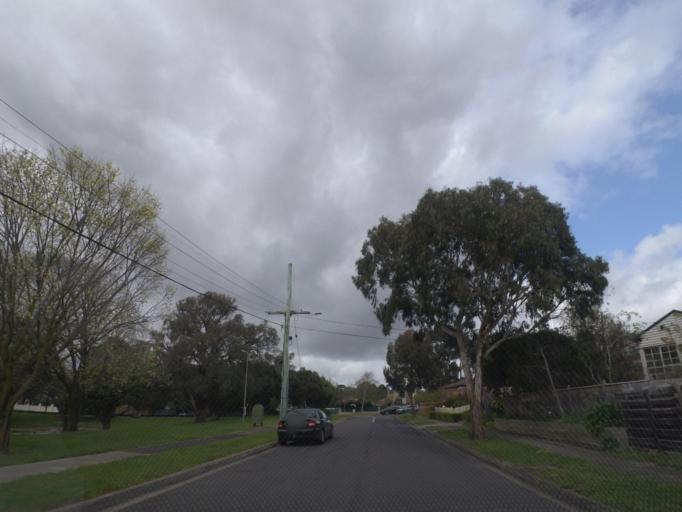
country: AU
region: Victoria
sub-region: Whitehorse
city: Blackburn
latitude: -37.8169
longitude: 145.1448
